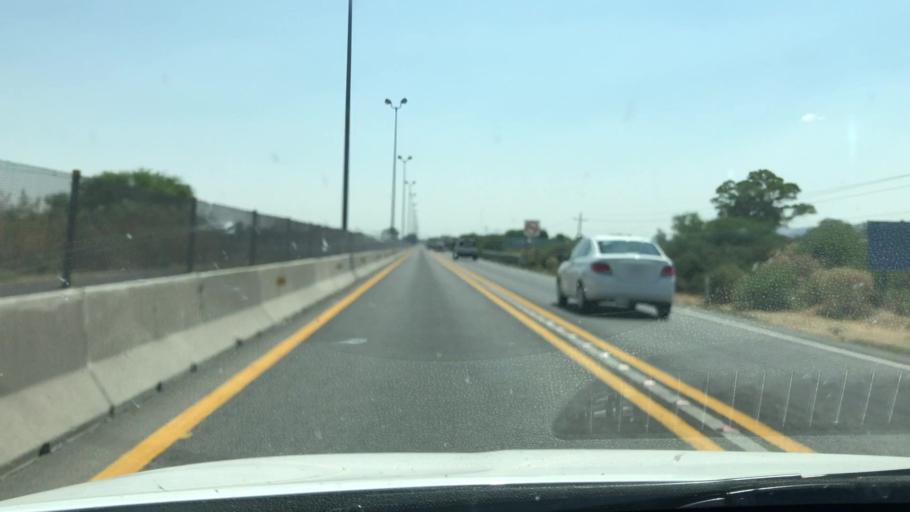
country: MX
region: Guanajuato
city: Abasolo
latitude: 20.4543
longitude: -101.5425
